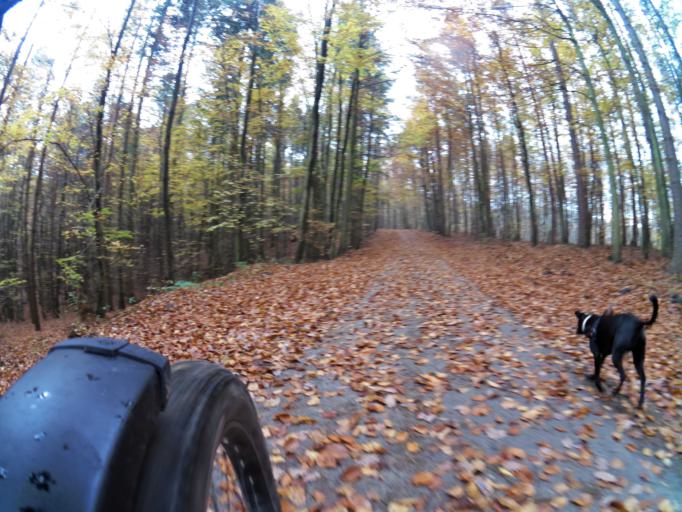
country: PL
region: Pomeranian Voivodeship
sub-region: Powiat pucki
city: Krokowa
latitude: 54.7731
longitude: 18.0922
